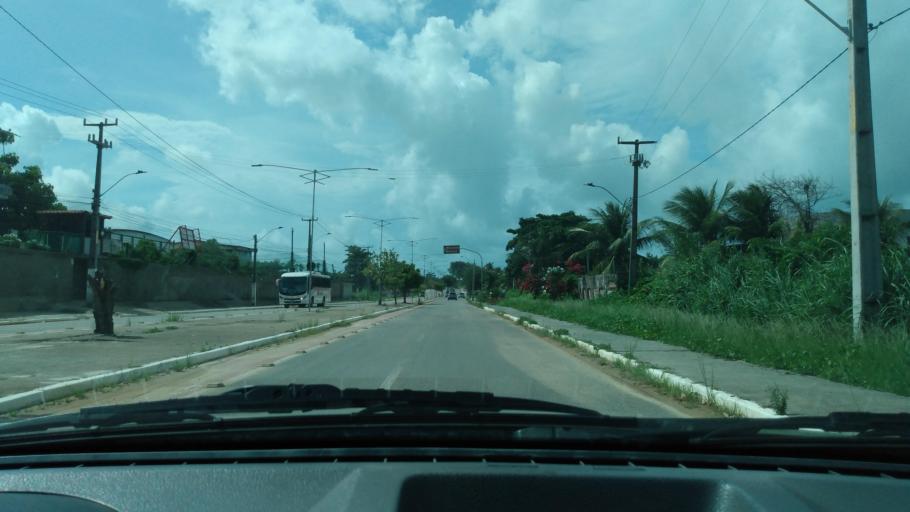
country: BR
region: Pernambuco
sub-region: Cabo De Santo Agostinho
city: Cabo
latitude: -8.3150
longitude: -34.9496
